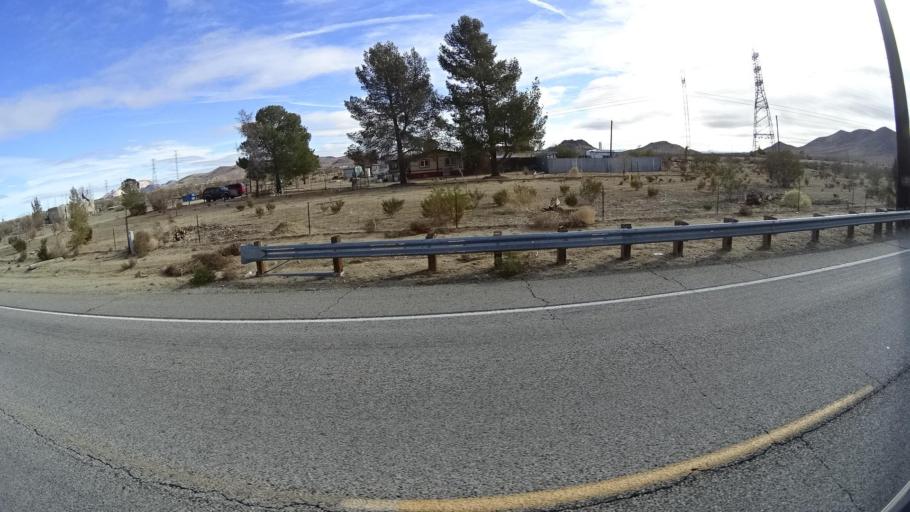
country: US
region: California
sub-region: Kern County
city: Rosamond
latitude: 34.9042
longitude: -118.2914
